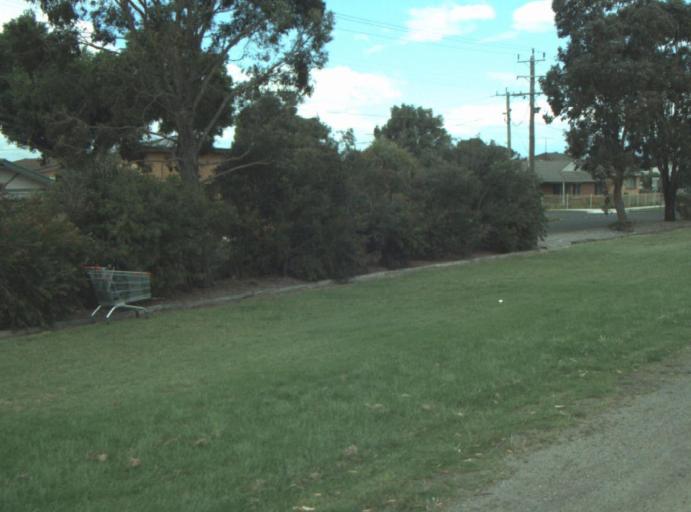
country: AU
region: Victoria
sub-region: Greater Geelong
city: Bell Park
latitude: -38.0694
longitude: 144.3587
